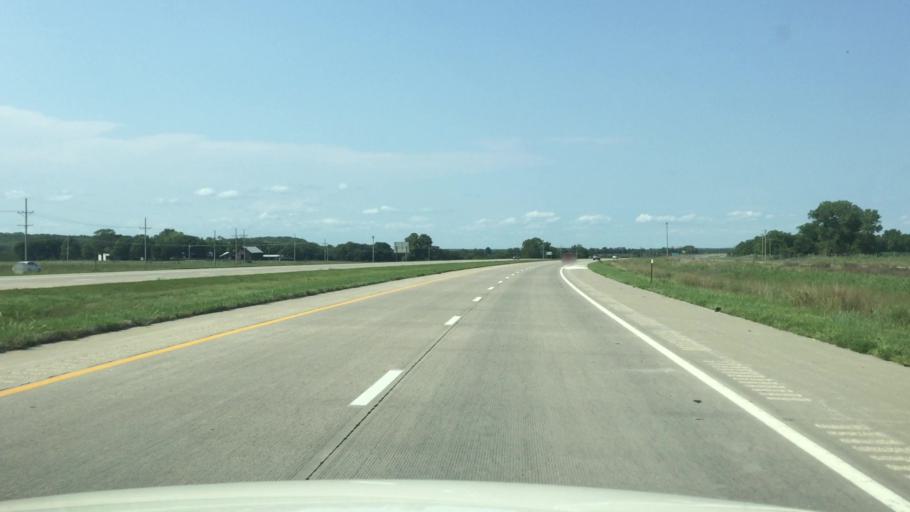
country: US
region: Kansas
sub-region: Linn County
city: Pleasanton
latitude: 38.1926
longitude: -94.7050
